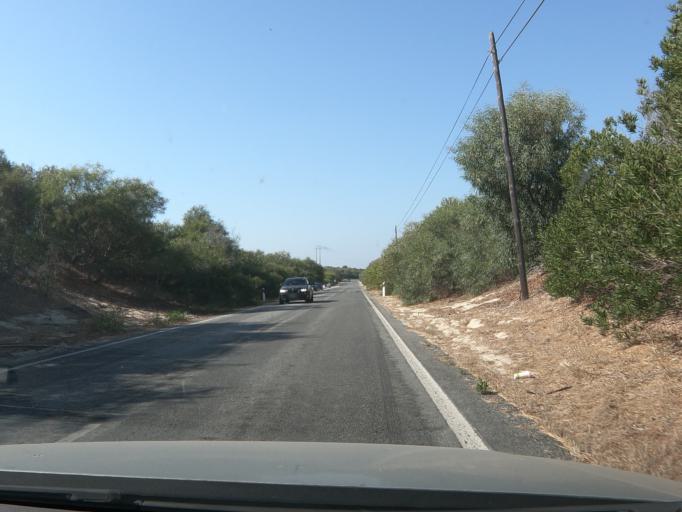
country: PT
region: Setubal
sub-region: Setubal
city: Setubal
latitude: 38.4093
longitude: -8.8120
